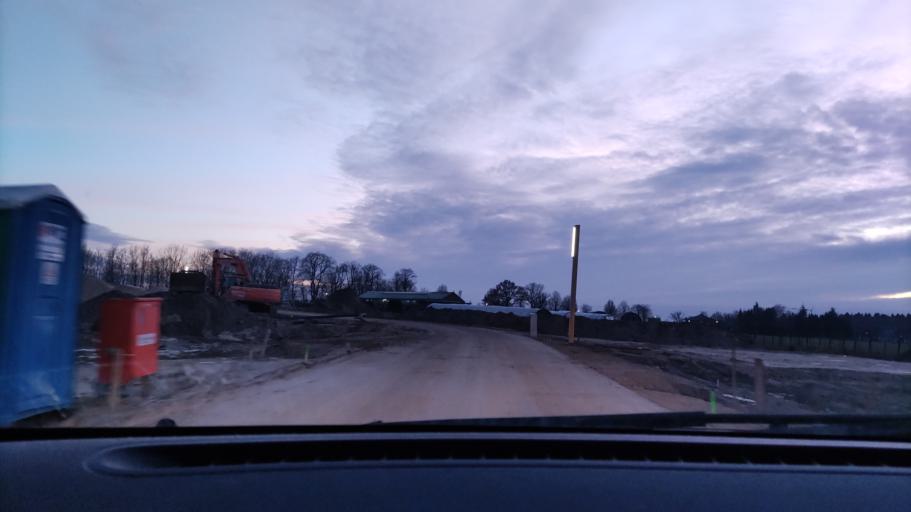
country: DE
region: Mecklenburg-Vorpommern
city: Boizenburg
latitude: 53.3779
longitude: 10.7024
